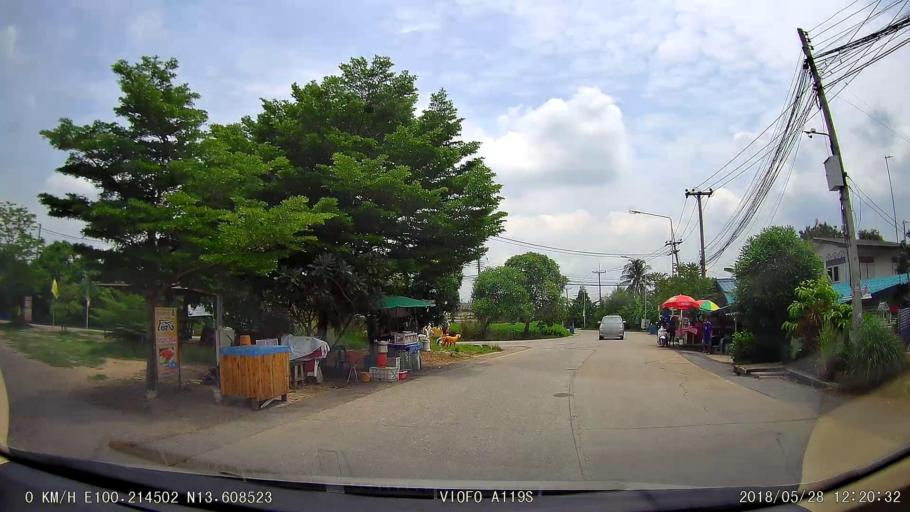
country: TH
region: Samut Sakhon
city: Krathum Baen
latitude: 13.6147
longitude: 100.2131
